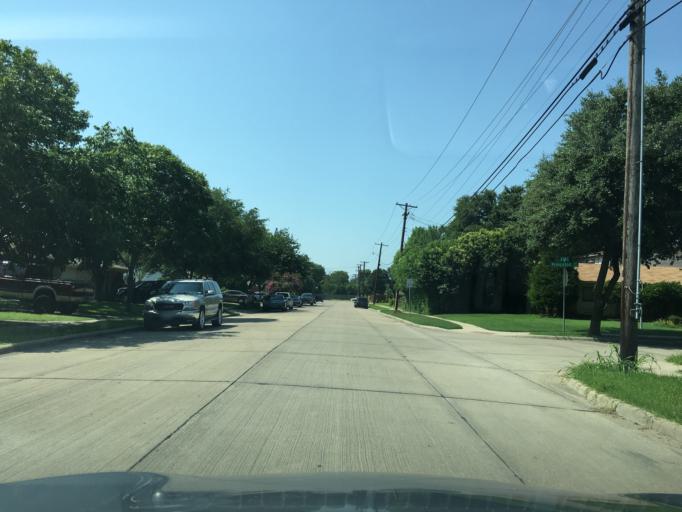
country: US
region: Texas
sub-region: Dallas County
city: Richardson
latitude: 32.9188
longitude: -96.6927
